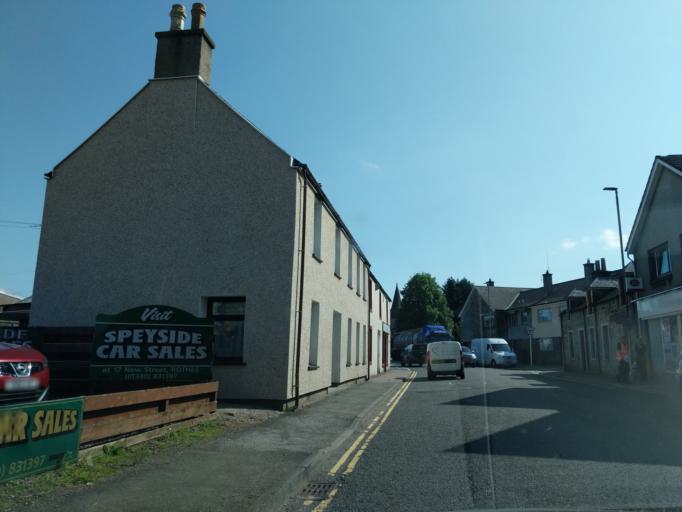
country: GB
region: Scotland
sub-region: Moray
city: Rothes
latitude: 57.5280
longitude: -3.2082
